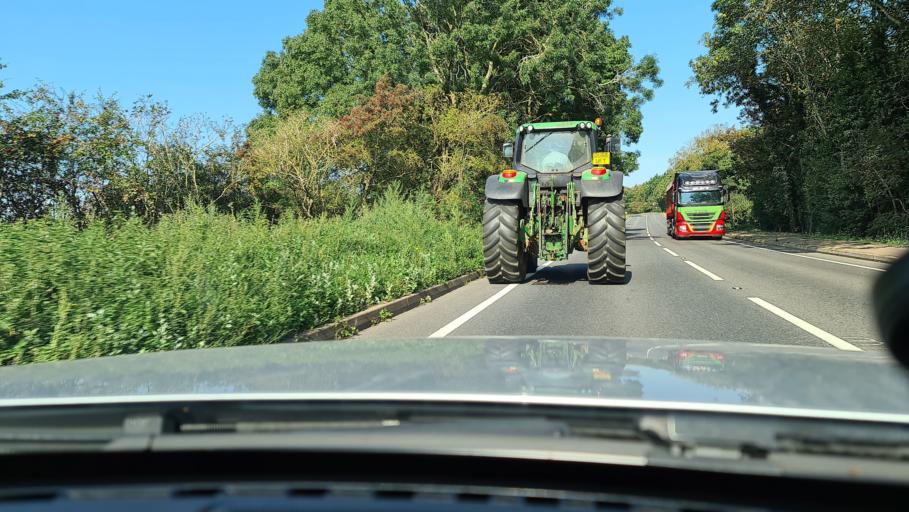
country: GB
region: England
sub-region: Northamptonshire
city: Bugbrooke
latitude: 52.2069
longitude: -1.0475
